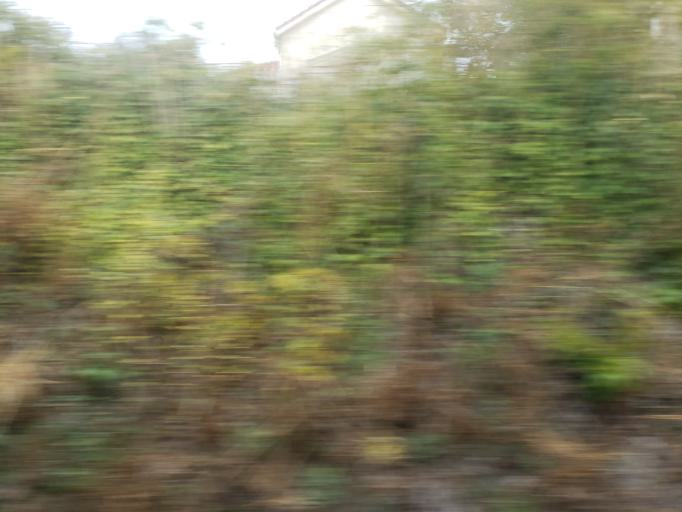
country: JP
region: Hyogo
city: Akashi
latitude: 34.6317
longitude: 135.0409
